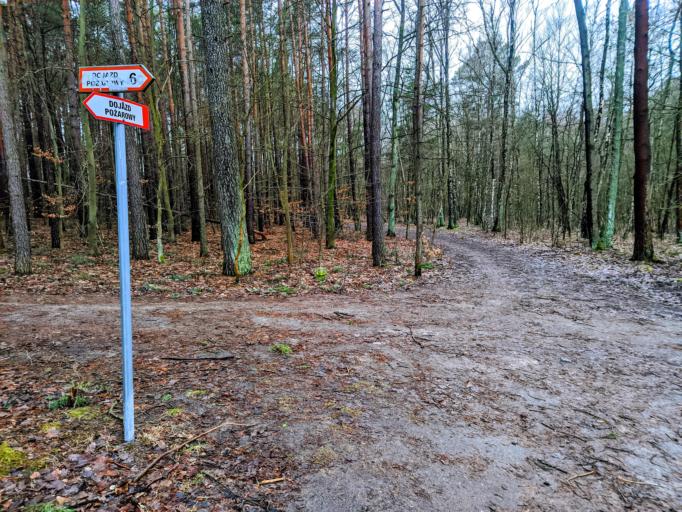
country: PL
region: Lubusz
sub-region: Zielona Gora
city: Zielona Gora
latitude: 51.9328
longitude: 15.5388
